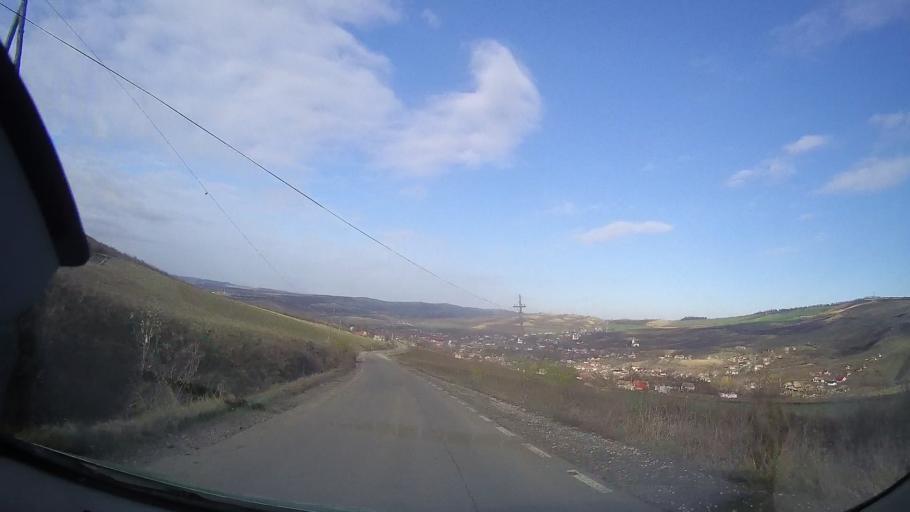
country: RO
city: Barza
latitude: 46.5473
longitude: 24.1470
